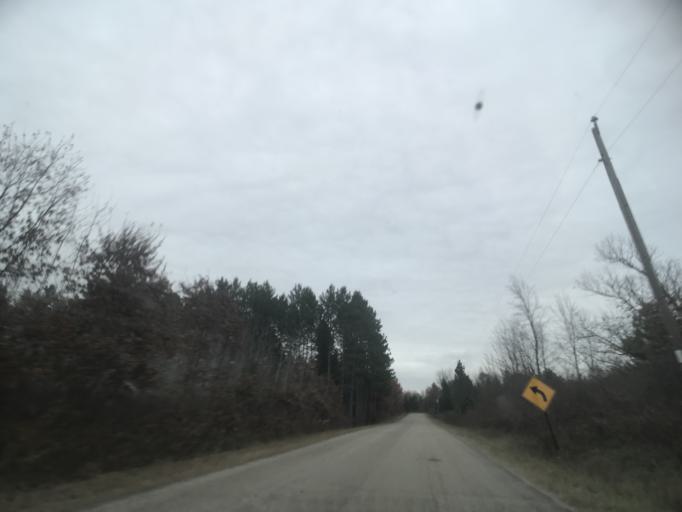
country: US
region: Wisconsin
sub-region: Oconto County
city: Gillett
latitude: 45.3155
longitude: -88.2766
